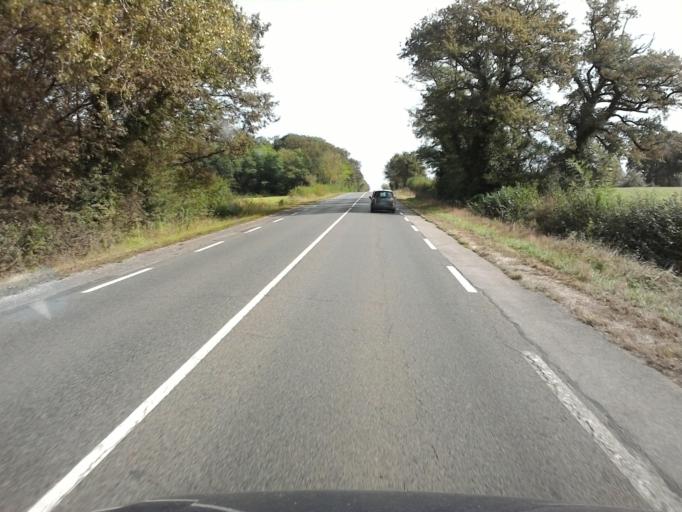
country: FR
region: Rhone-Alpes
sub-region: Departement de l'Ain
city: Saint-Denis-les-Bourg
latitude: 46.2369
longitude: 5.1747
